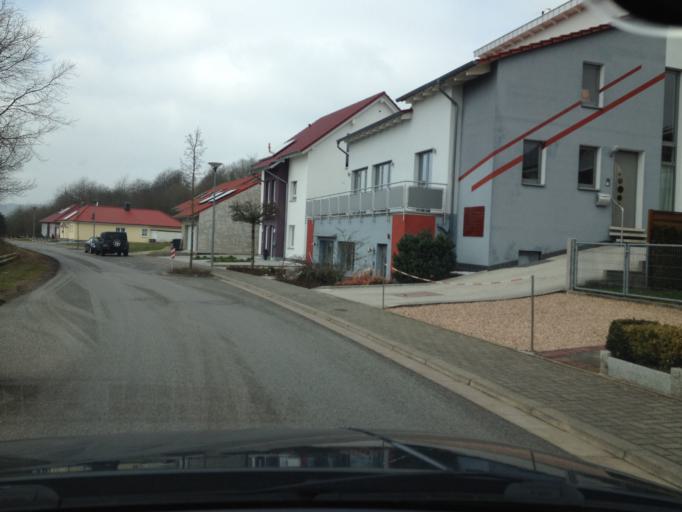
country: DE
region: Saarland
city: Ottweiler
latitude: 49.3982
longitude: 7.1799
